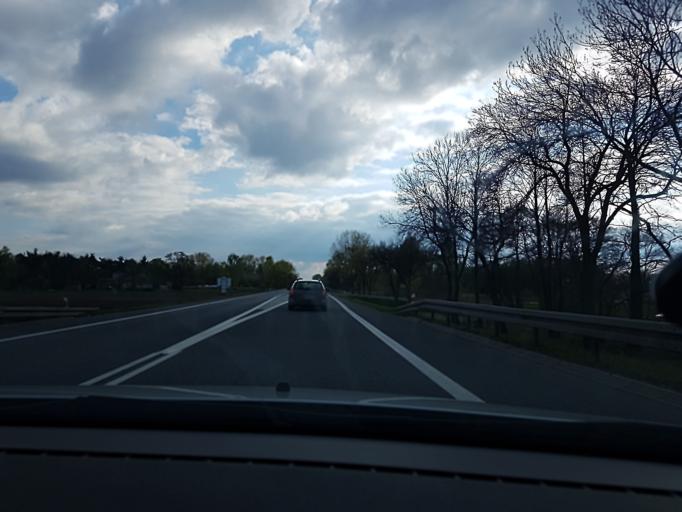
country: PL
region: Masovian Voivodeship
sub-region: Powiat sochaczewski
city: Sochaczew
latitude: 52.2039
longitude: 20.1780
